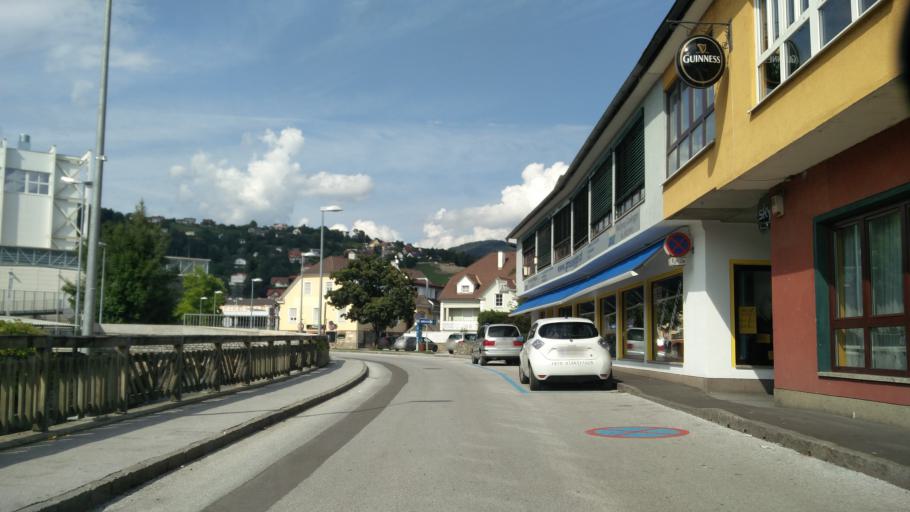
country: AT
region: Styria
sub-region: Politischer Bezirk Weiz
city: Weiz
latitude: 47.2197
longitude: 15.6242
